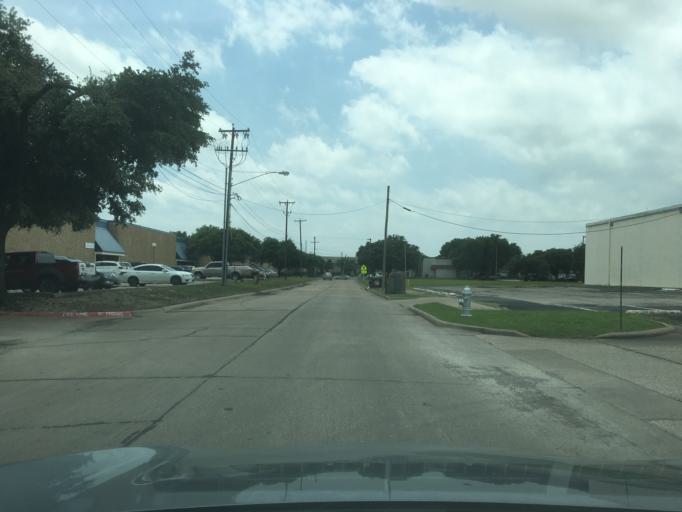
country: US
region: Texas
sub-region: Dallas County
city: Garland
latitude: 32.9154
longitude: -96.6787
